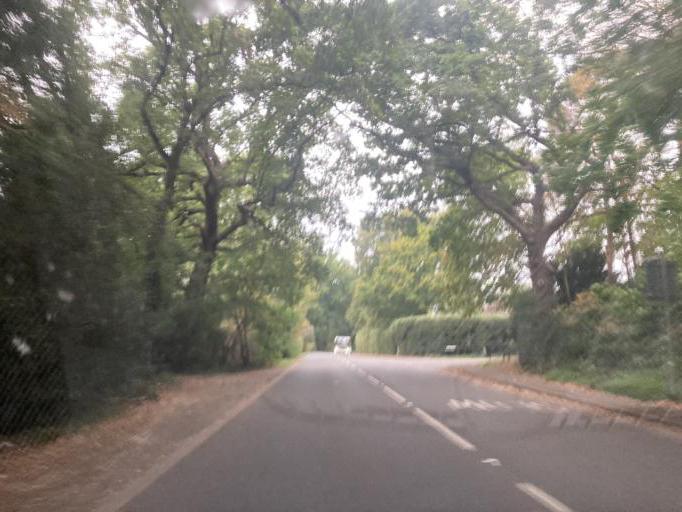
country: GB
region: England
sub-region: Surrey
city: Windlesham
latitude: 51.3700
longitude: -0.6701
